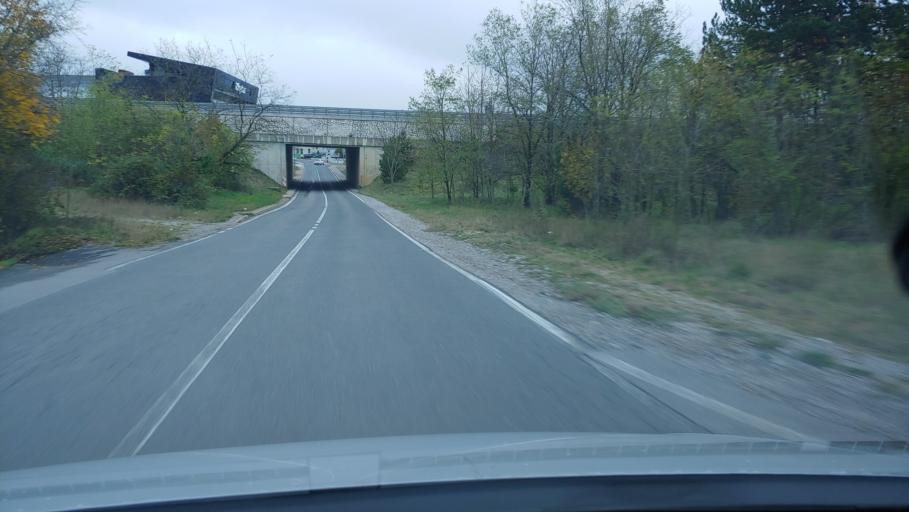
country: SI
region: Sezana
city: Sezana
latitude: 45.7107
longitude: 13.8534
